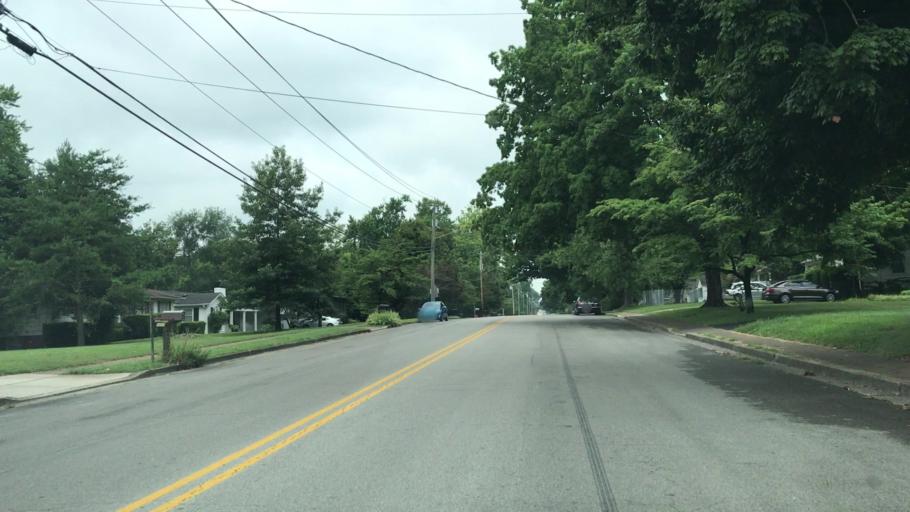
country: US
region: Kentucky
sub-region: Warren County
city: Bowling Green
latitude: 36.9847
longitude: -86.4205
